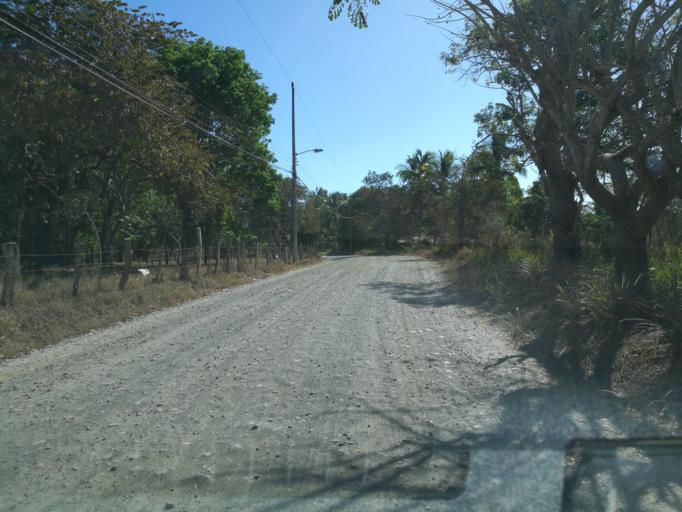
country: CR
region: Puntarenas
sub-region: Canton Central de Puntarenas
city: Puntarenas
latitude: 10.0915
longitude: -84.9637
